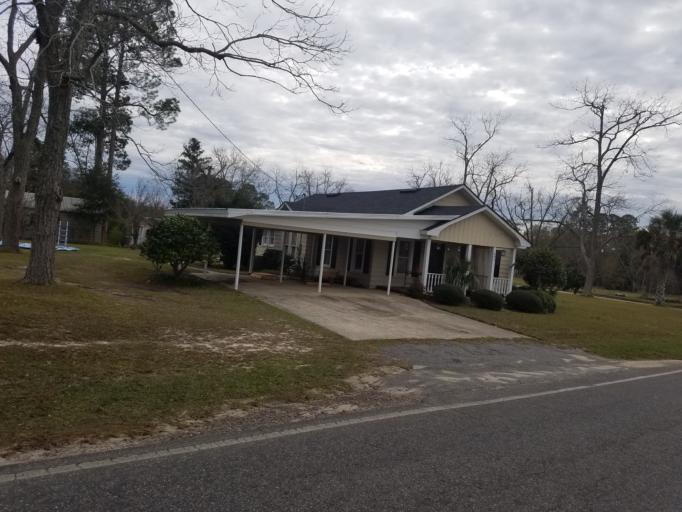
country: US
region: Georgia
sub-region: Berrien County
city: Nashville
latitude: 31.2159
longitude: -83.2560
